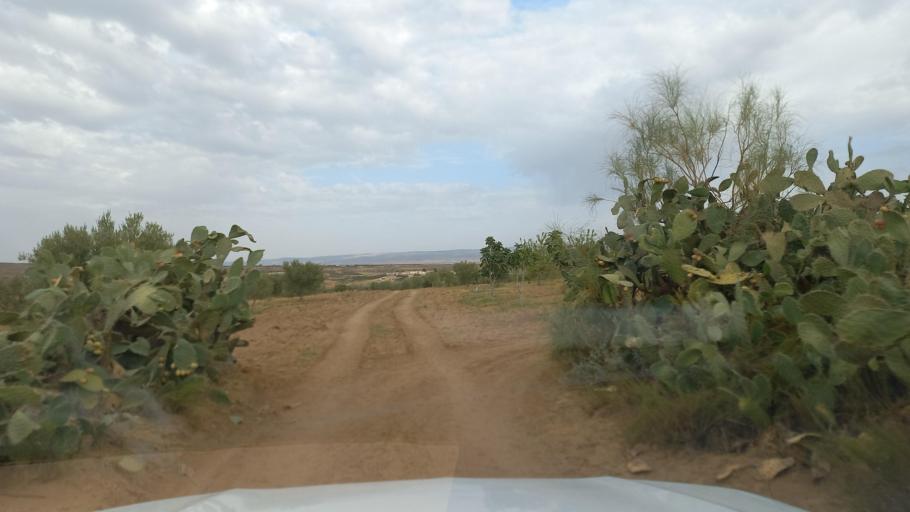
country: TN
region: Al Qasrayn
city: Kasserine
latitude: 35.1939
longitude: 9.0471
